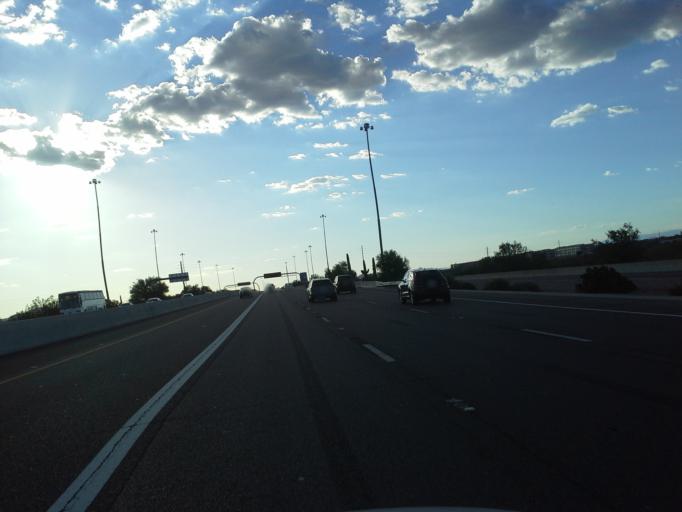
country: US
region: Arizona
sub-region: Maricopa County
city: Paradise Valley
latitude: 33.6660
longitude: -111.9559
